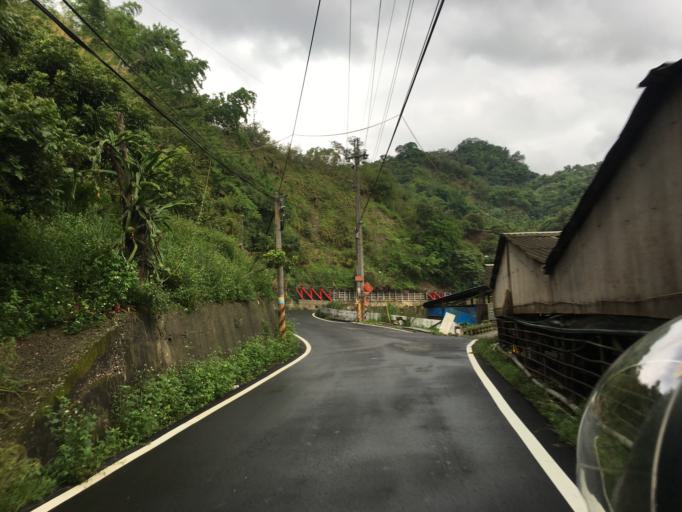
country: TW
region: Taiwan
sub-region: Taichung City
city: Taichung
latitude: 24.0607
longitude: 120.7413
